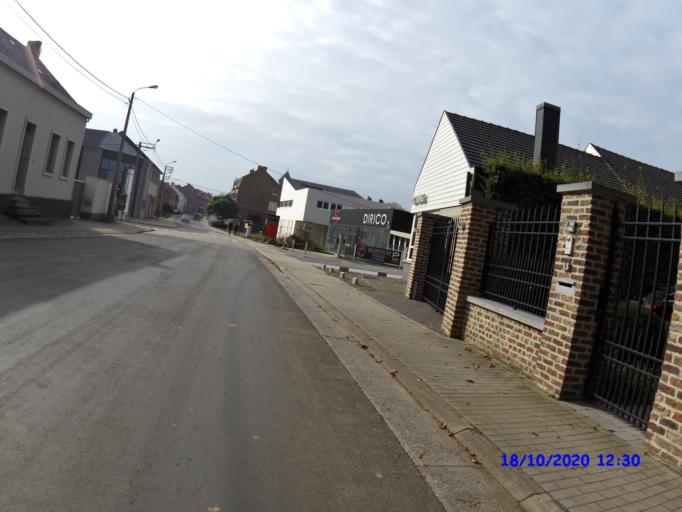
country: BE
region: Flanders
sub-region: Provincie Vlaams-Brabant
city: Landen
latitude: 50.7679
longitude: 5.0406
